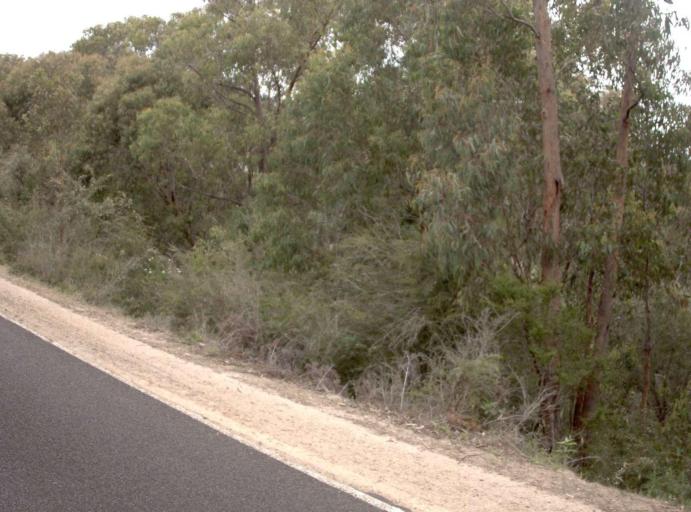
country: AU
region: Victoria
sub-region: Latrobe
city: Traralgon
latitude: -38.3940
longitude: 146.8116
